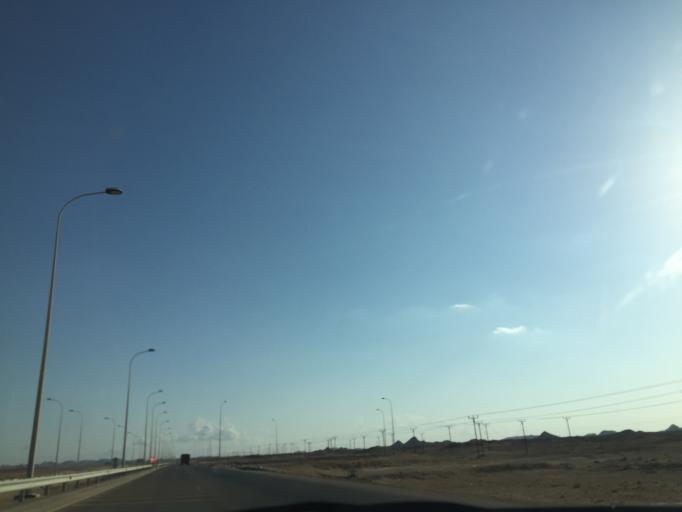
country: OM
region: Zufar
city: Salalah
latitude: 17.5330
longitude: 54.0555
